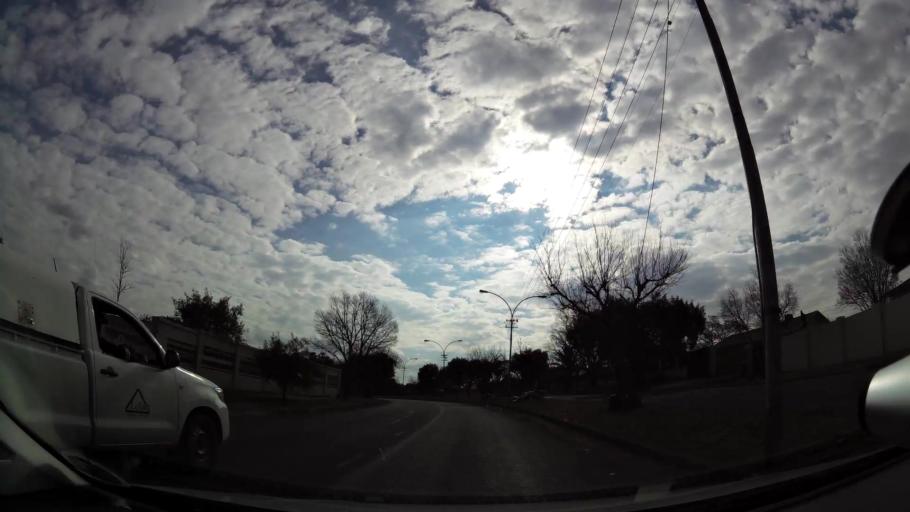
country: ZA
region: Orange Free State
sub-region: Mangaung Metropolitan Municipality
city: Bloemfontein
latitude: -29.0750
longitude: 26.2424
